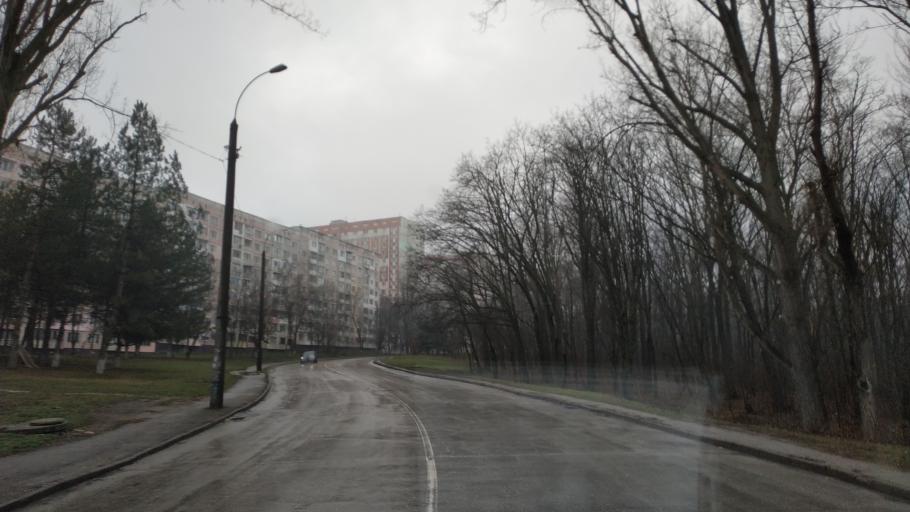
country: MD
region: Chisinau
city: Vatra
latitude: 47.0394
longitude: 28.7795
